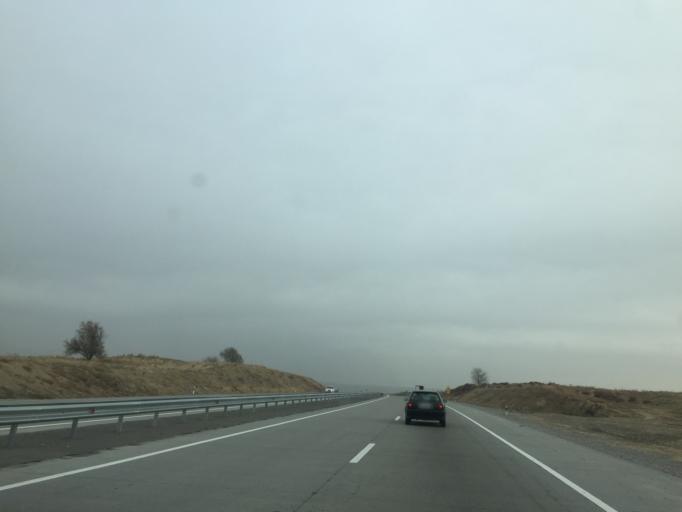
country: KZ
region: Ongtustik Qazaqstan
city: Aksu
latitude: 42.4508
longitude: 69.7457
